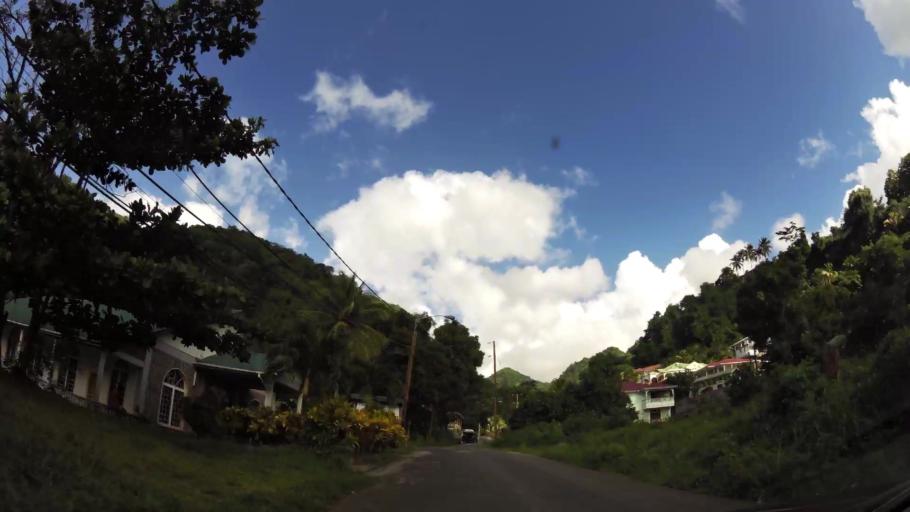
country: DM
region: Saint George
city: Roseau
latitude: 15.2856
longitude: -61.3729
